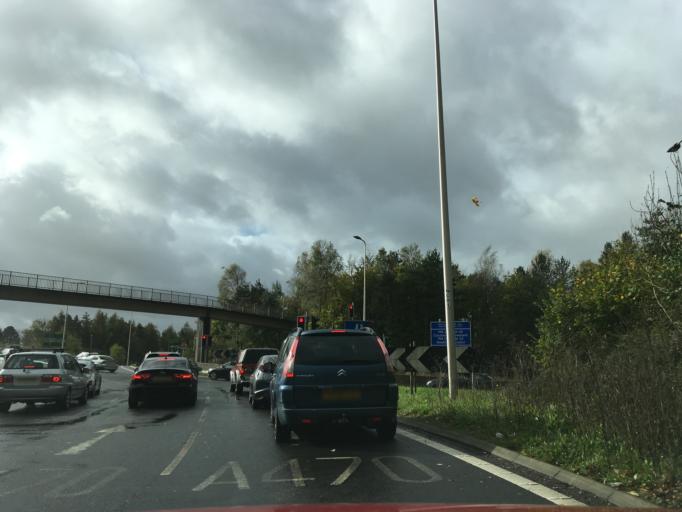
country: GB
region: Wales
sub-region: Cardiff
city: Radyr
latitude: 51.5278
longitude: -3.2368
